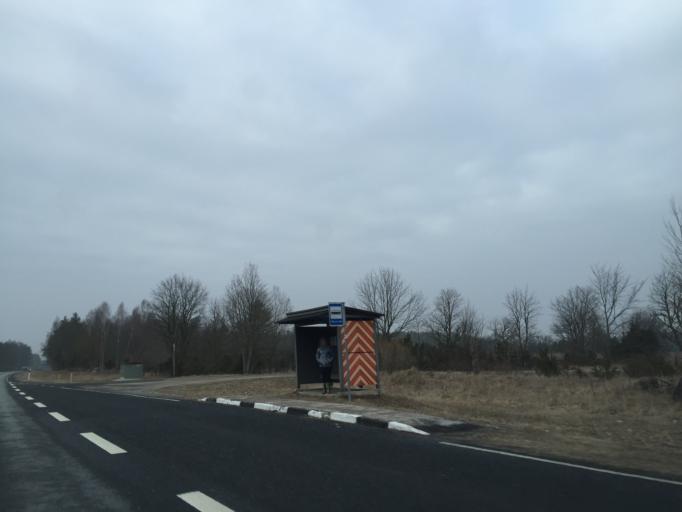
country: EE
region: Saare
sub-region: Orissaare vald
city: Orissaare
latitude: 58.5919
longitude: 23.3332
